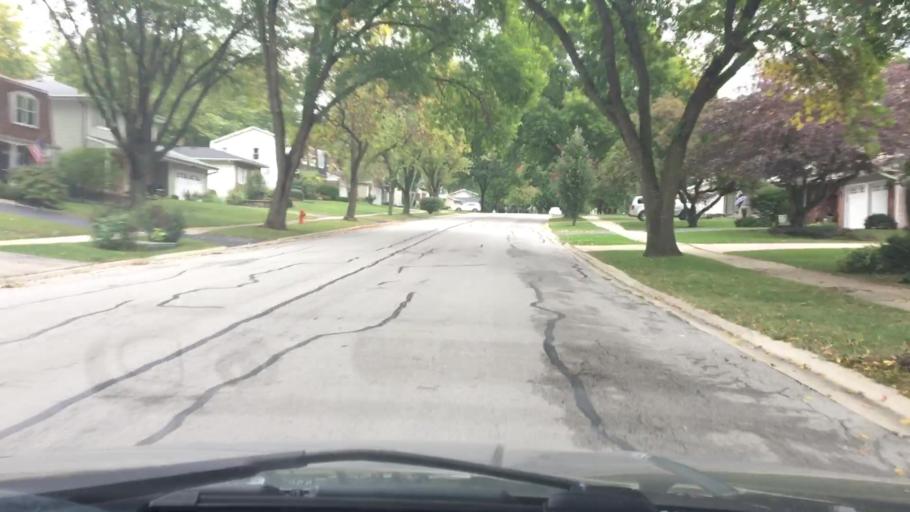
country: US
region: Illinois
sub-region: DuPage County
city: Naperville
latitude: 41.7428
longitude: -88.1354
